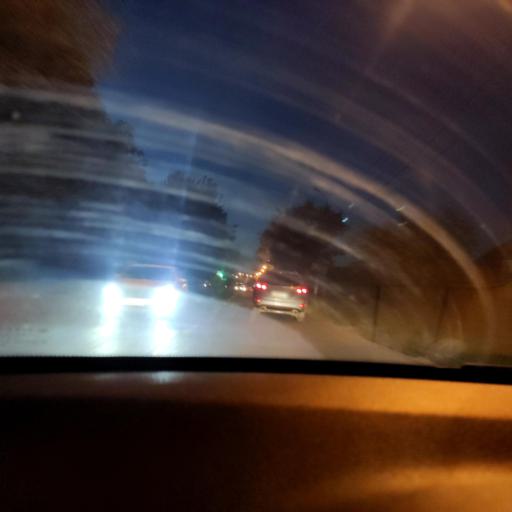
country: RU
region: Samara
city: Samara
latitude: 53.1749
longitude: 50.1715
